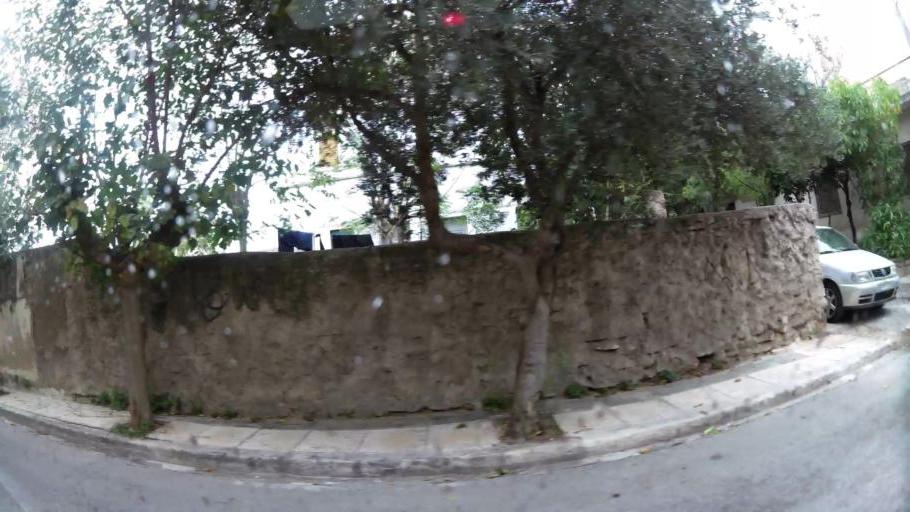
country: GR
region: Attica
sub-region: Nomarchia Athinas
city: Agioi Anargyroi
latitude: 38.0197
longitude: 23.7127
